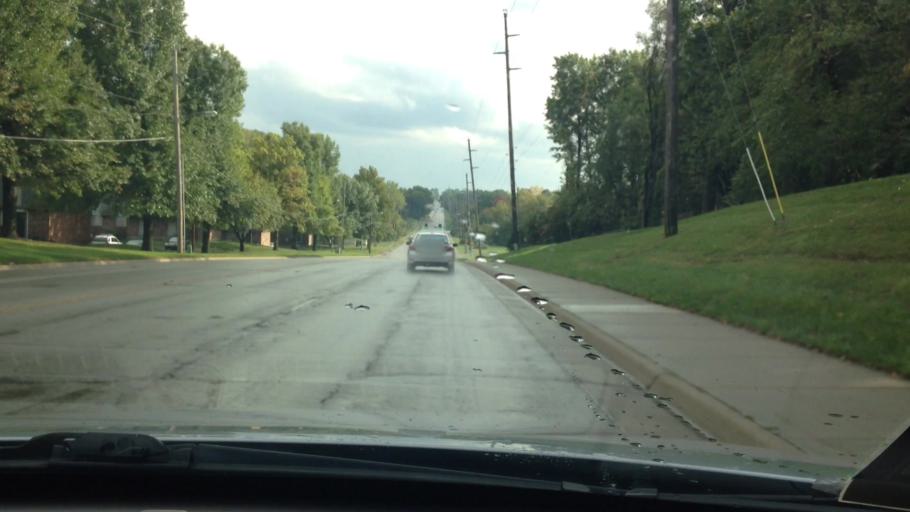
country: US
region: Kansas
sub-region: Leavenworth County
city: Leavenworth
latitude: 39.2846
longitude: -94.9279
